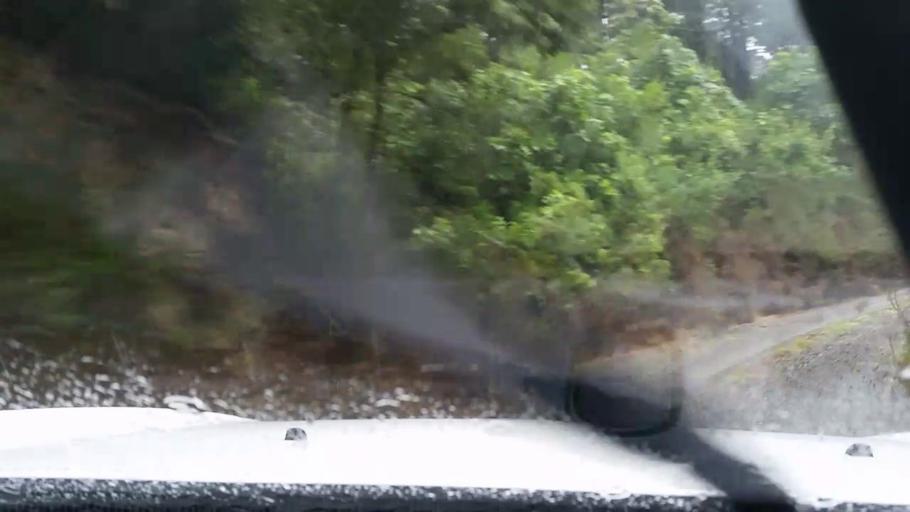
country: NZ
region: Wellington
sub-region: Masterton District
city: Masterton
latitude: -41.1590
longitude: 175.8022
